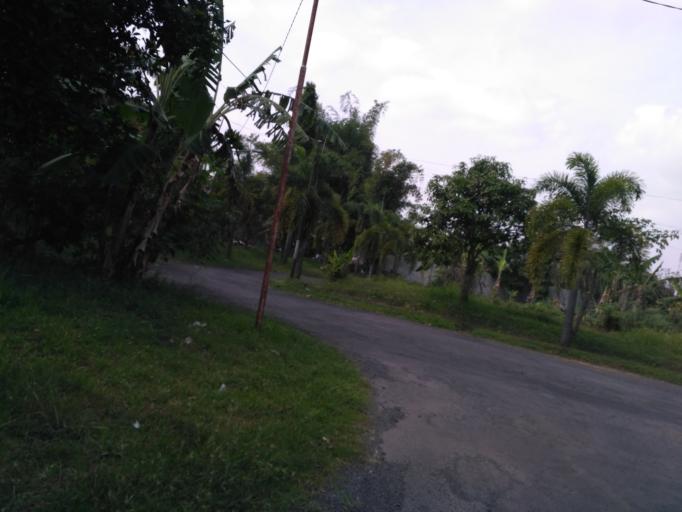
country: ID
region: East Java
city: Malang
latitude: -7.9294
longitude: 112.6130
